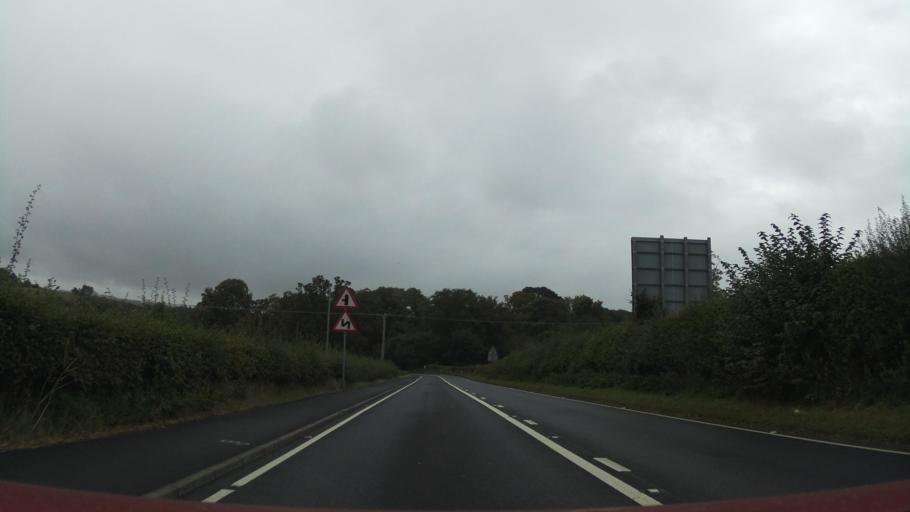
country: GB
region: Scotland
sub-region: The Scottish Borders
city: Jedburgh
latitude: 55.5012
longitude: -2.5454
